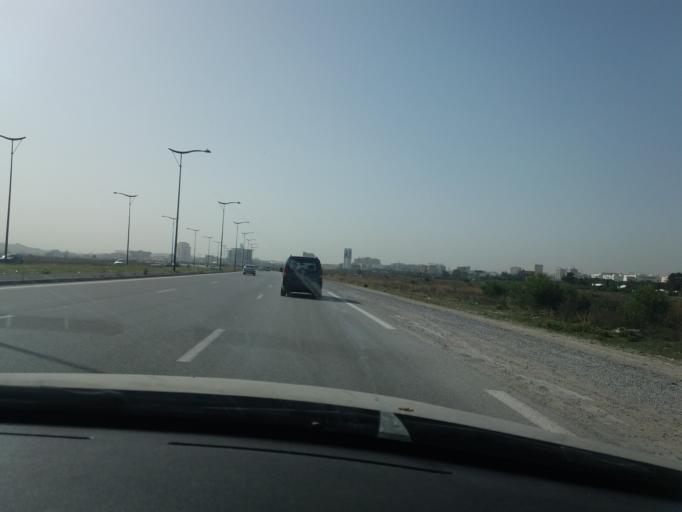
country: TN
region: Tunis
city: Tunis
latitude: 36.8196
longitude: 10.1987
